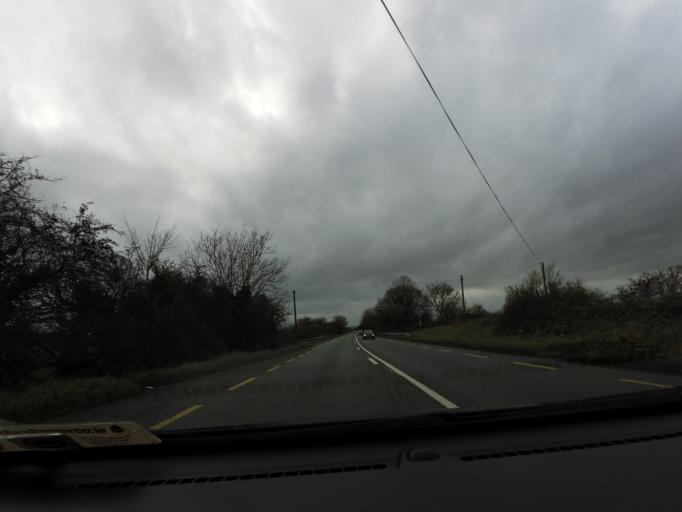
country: IE
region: Leinster
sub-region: Kilkenny
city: Ballyragget
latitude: 52.7730
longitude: -7.3312
